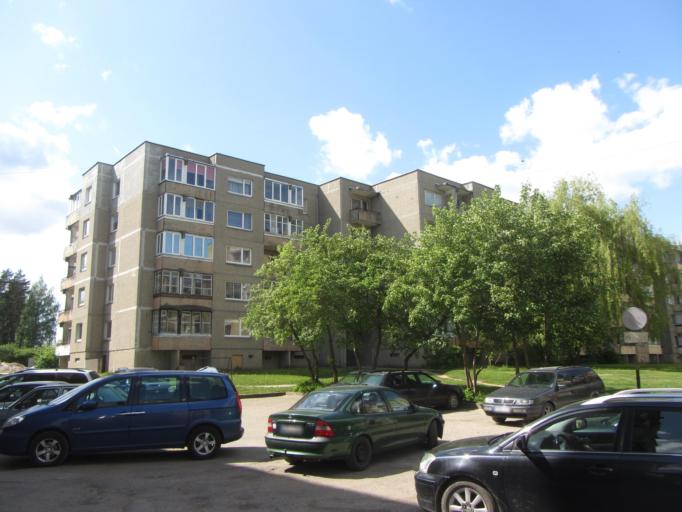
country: LT
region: Utenos apskritis
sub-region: Utena
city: Utena
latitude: 55.5093
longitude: 25.5837
